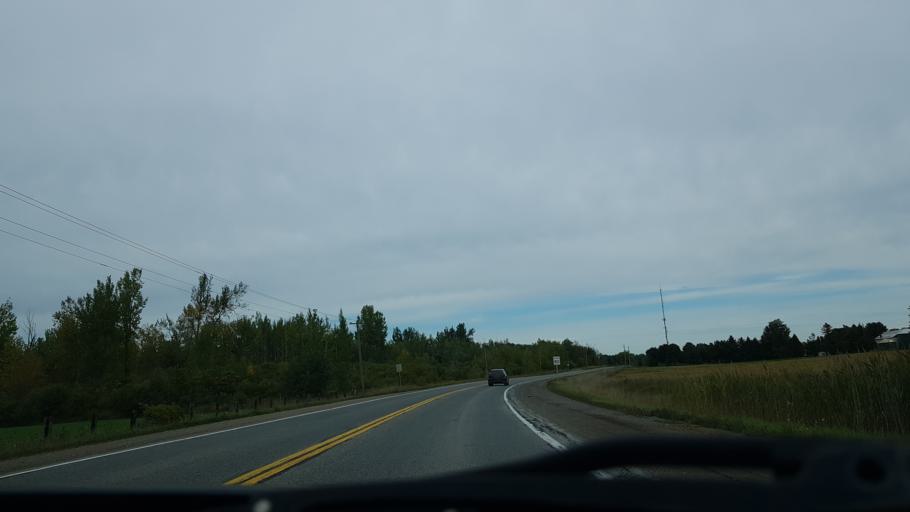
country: CA
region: Ontario
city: Orangeville
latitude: 43.9035
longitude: -79.9480
